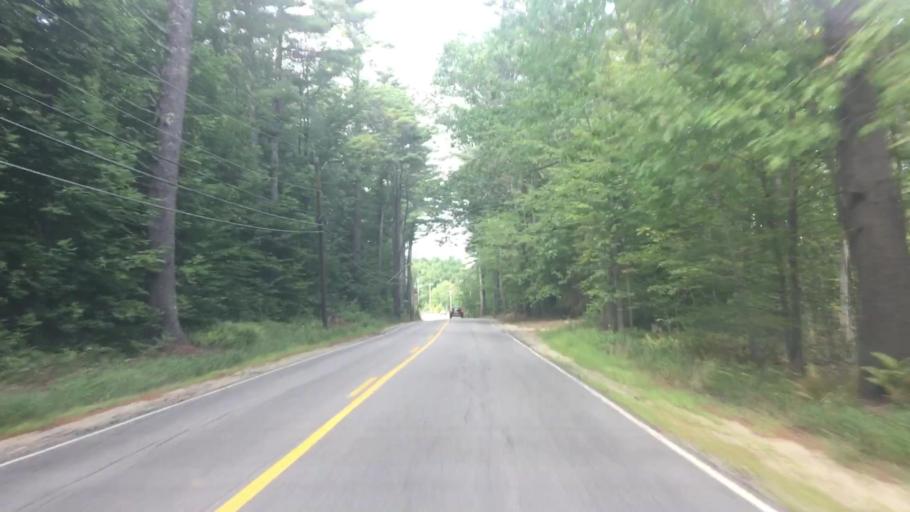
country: US
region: Maine
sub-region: Oxford County
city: Oxford
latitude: 44.1189
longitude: -70.5056
